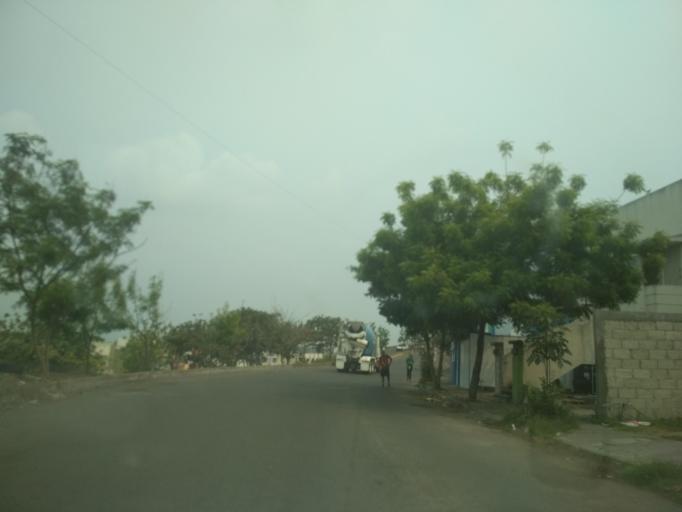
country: MX
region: Veracruz
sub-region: Veracruz
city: Fraccionamiento Geovillas los Pinos
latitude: 19.2239
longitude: -96.2365
